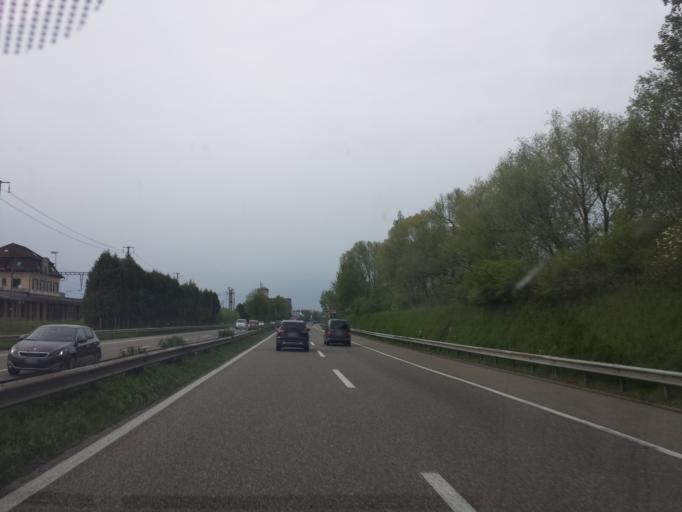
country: CH
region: Saint Gallen
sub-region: Wahlkreis Rheintal
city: Rheineck
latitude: 47.4661
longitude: 9.5922
